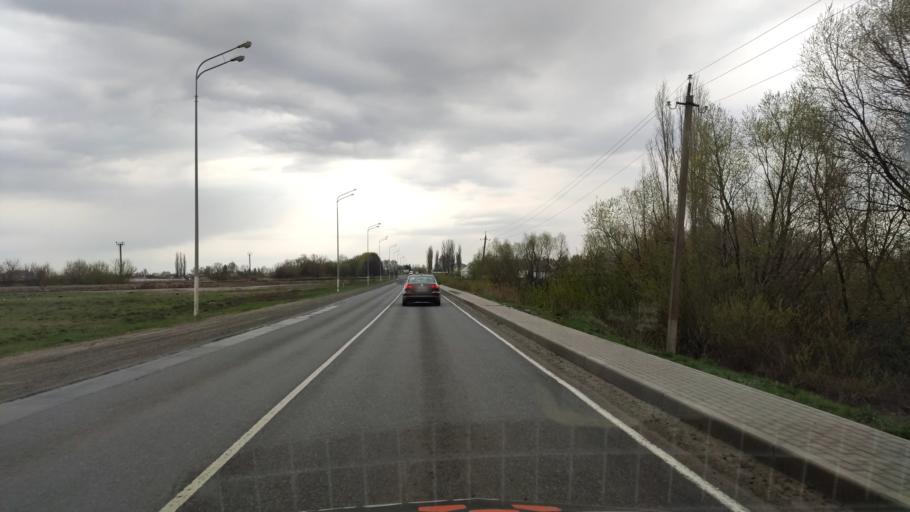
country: RU
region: Kursk
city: Gorshechnoye
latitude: 51.5310
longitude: 38.0221
